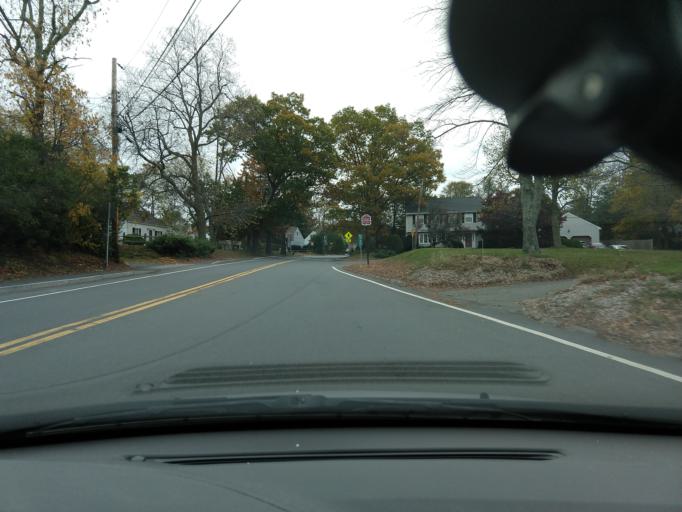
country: US
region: Massachusetts
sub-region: Middlesex County
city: Lexington
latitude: 42.4420
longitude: -71.2538
